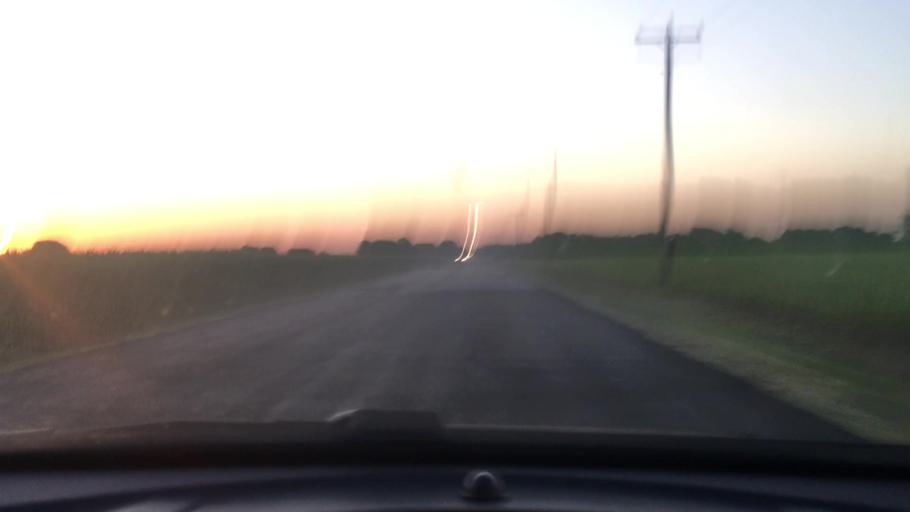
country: US
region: Texas
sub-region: Ellis County
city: Red Oak
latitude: 32.5607
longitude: -96.8034
